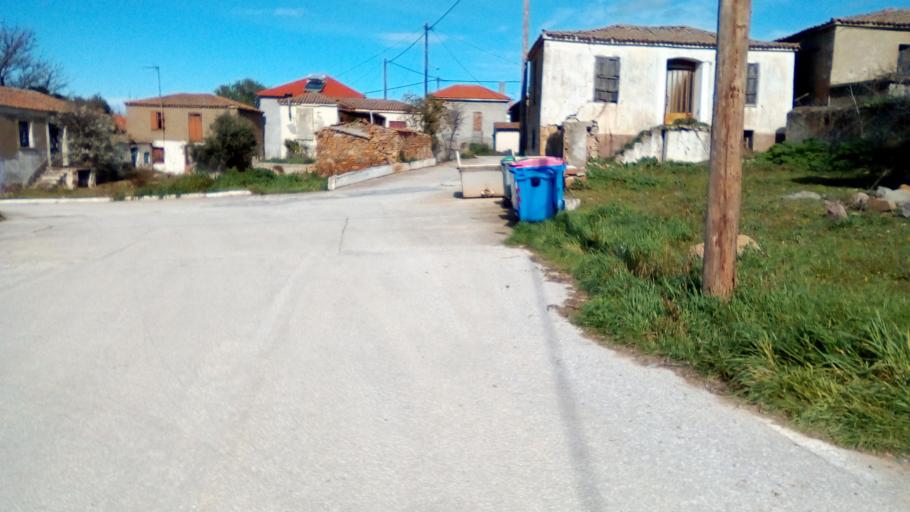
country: GR
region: North Aegean
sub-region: Nomos Lesvou
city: Myrina
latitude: 39.9328
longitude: 25.2313
